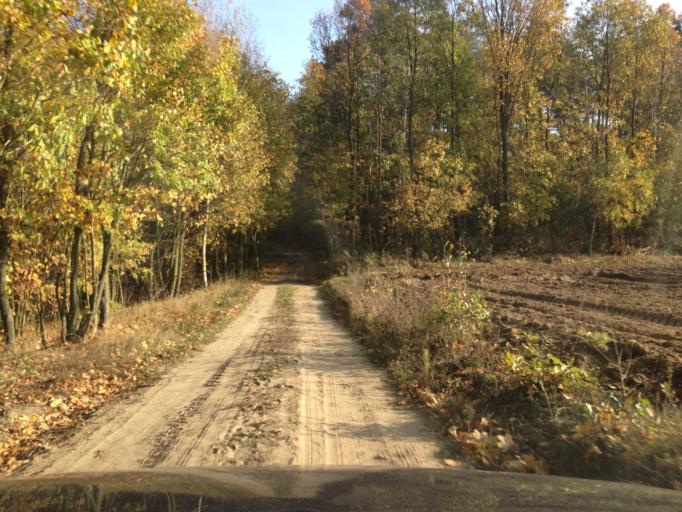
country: PL
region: Kujawsko-Pomorskie
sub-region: Powiat brodnicki
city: Gorzno
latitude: 53.2718
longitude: 19.7085
